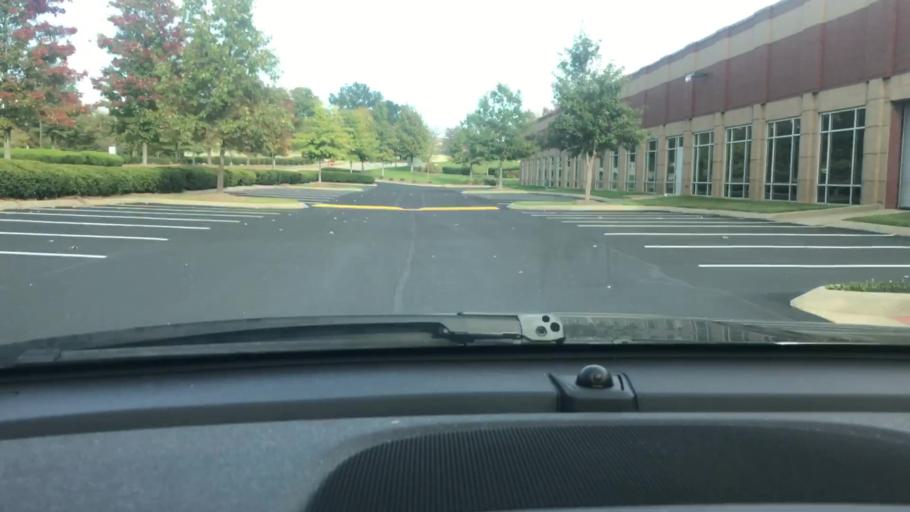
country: US
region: Tennessee
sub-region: Williamson County
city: Franklin
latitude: 35.9513
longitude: -86.8336
